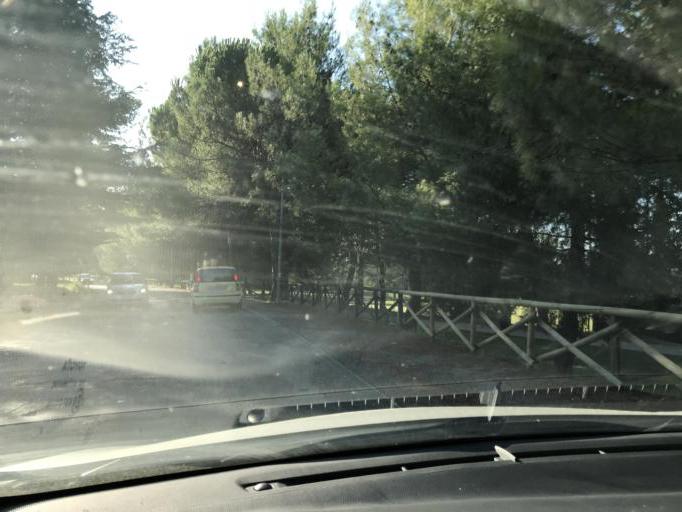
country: IT
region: Umbria
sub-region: Provincia di Perugia
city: Lacugnano
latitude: 43.1151
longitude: 12.3545
